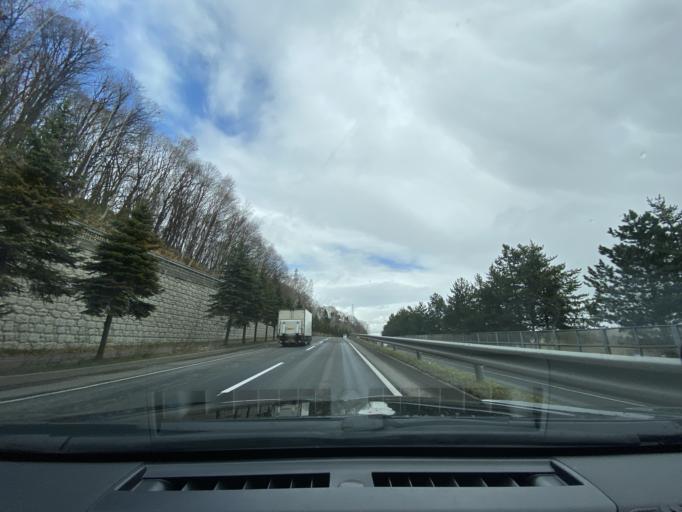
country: JP
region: Hokkaido
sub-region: Asahikawa-shi
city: Asahikawa
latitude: 43.8109
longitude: 142.3627
